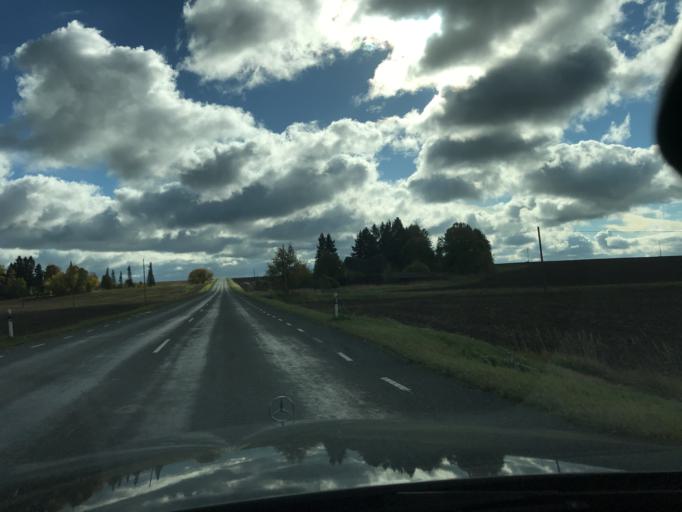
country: EE
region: Vorumaa
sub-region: Antsla vald
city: Vana-Antsla
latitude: 57.9226
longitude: 26.3439
